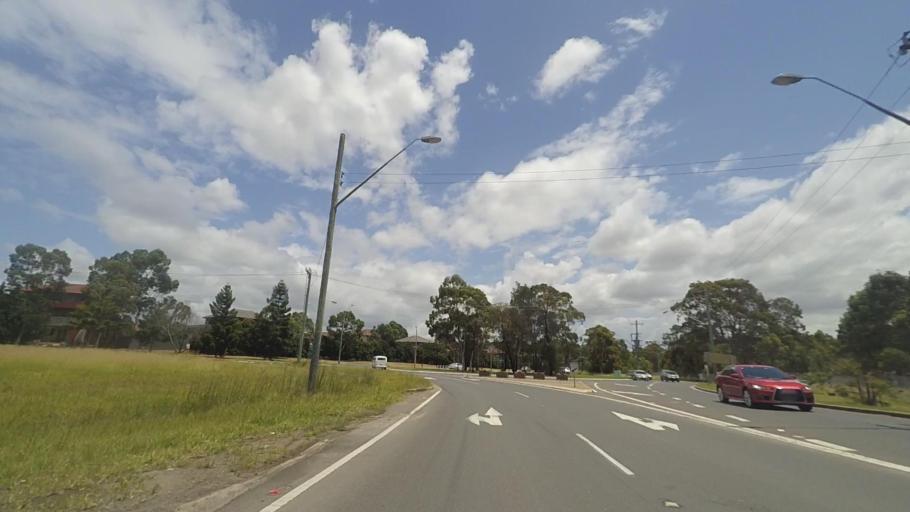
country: AU
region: New South Wales
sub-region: Liverpool
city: Holsworthy
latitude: -33.9615
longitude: 150.9602
